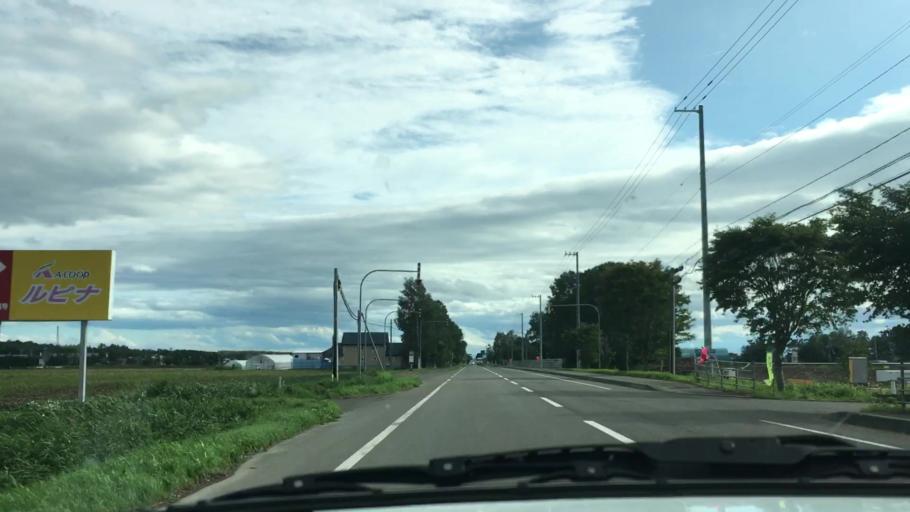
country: JP
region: Hokkaido
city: Otofuke
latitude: 43.2449
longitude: 143.2978
